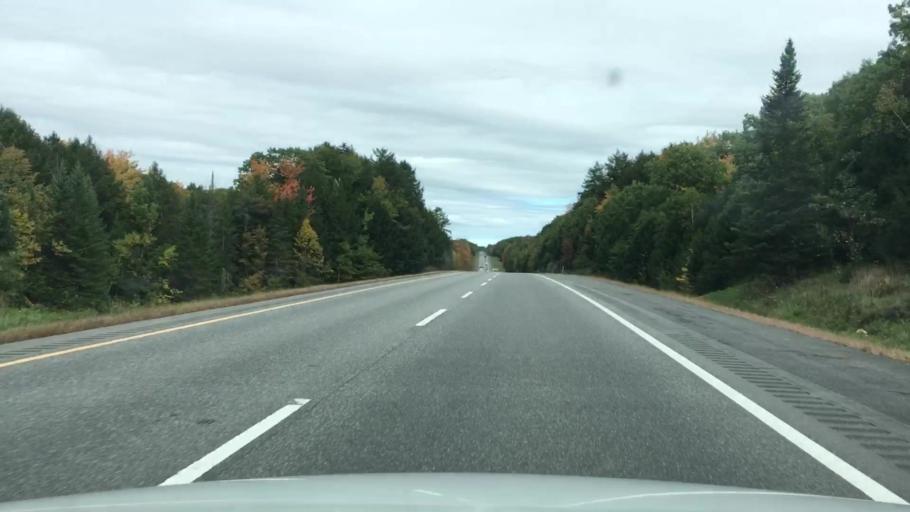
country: US
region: Maine
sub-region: Kennebec County
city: Sidney
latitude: 44.3961
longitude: -69.7549
